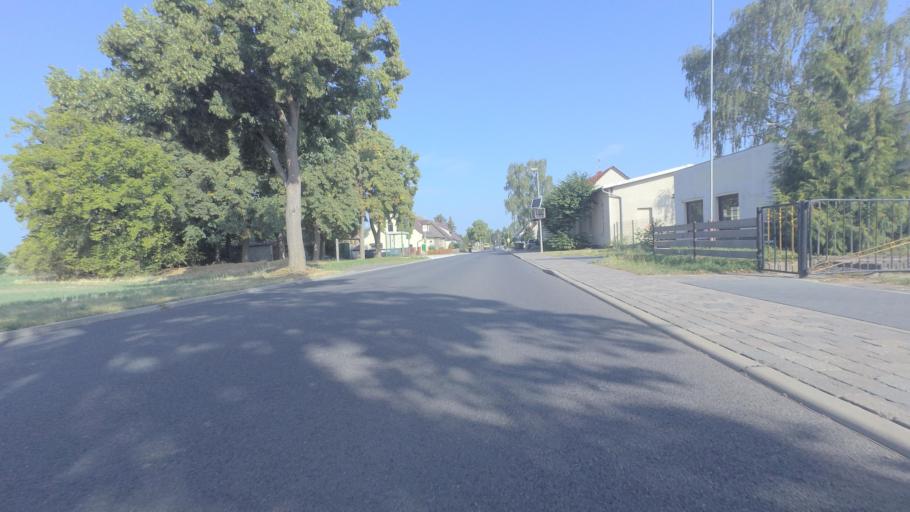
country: DE
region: Brandenburg
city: Fehrbellin
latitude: 52.7946
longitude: 12.8062
